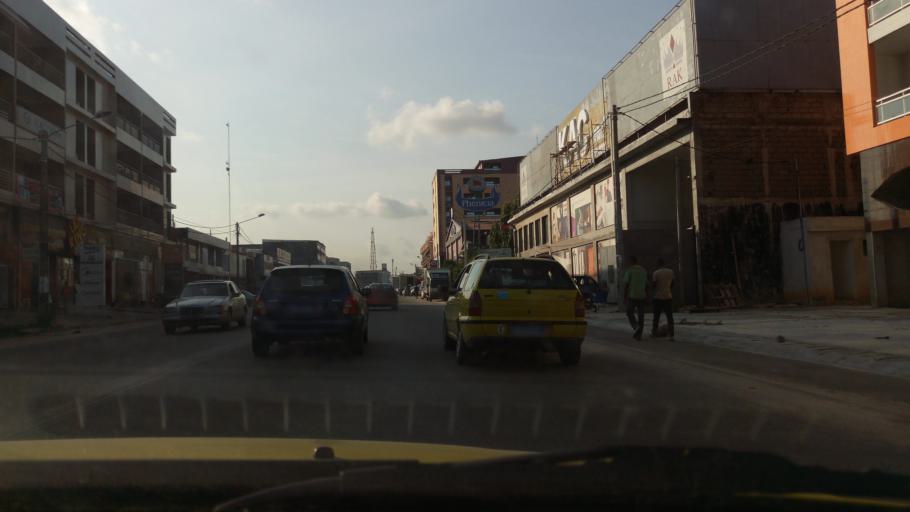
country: CI
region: Lagunes
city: Abobo
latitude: 5.3959
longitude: -3.9771
